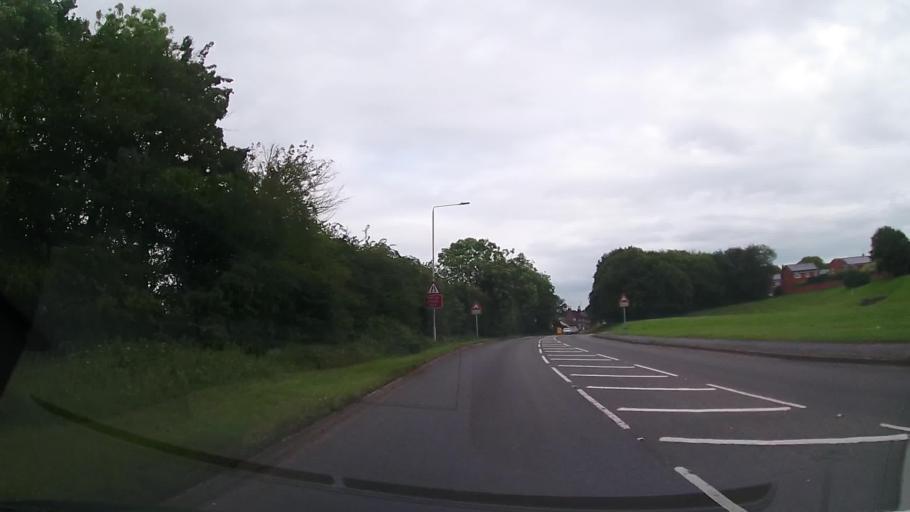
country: GB
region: England
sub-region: Leicestershire
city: Glenfield
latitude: 52.6482
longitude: -1.2120
